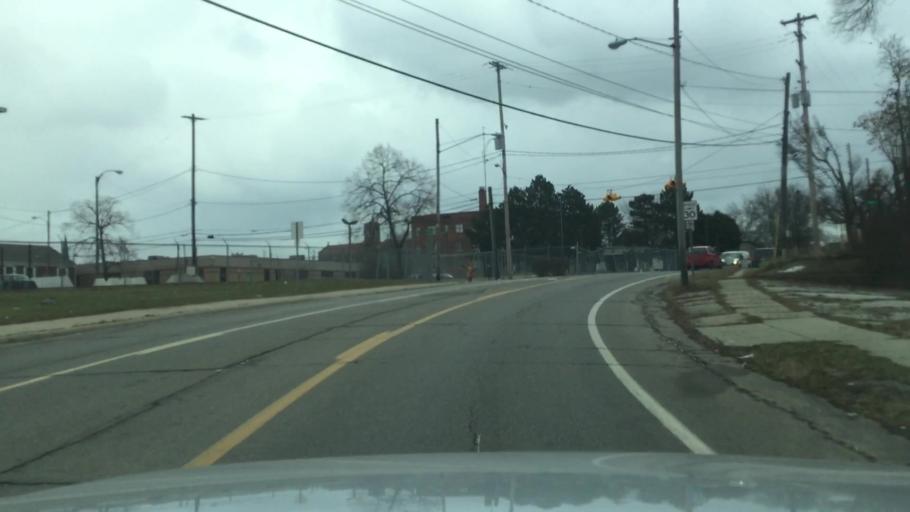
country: US
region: Michigan
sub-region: Genesee County
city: Flint
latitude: 43.0145
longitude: -83.6951
